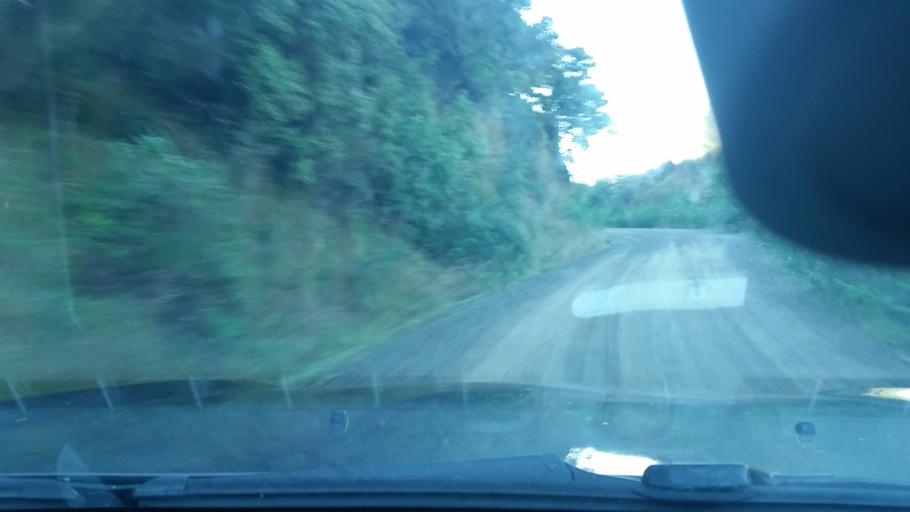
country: NZ
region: Marlborough
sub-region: Marlborough District
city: Blenheim
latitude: -41.5796
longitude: 174.0628
